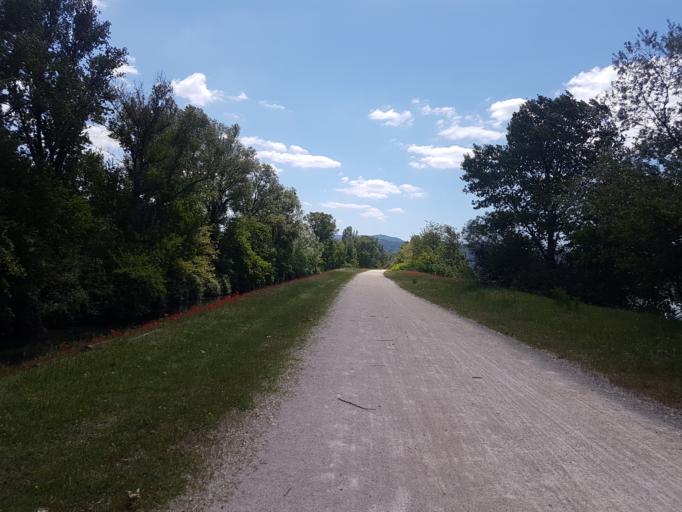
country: FR
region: Rhone-Alpes
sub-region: Departement de l'Ardeche
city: Tournon-sur-Rhone
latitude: 45.0487
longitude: 4.8584
